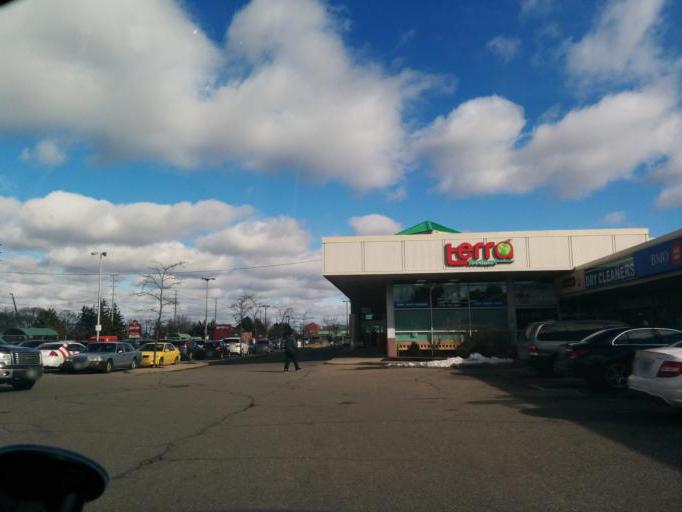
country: CA
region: Ontario
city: Mississauga
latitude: 43.5269
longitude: -79.6759
